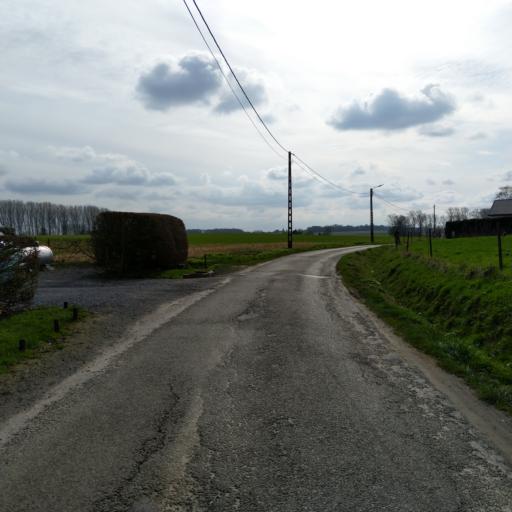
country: BE
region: Wallonia
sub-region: Province du Hainaut
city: Soignies
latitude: 50.5386
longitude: 4.0615
